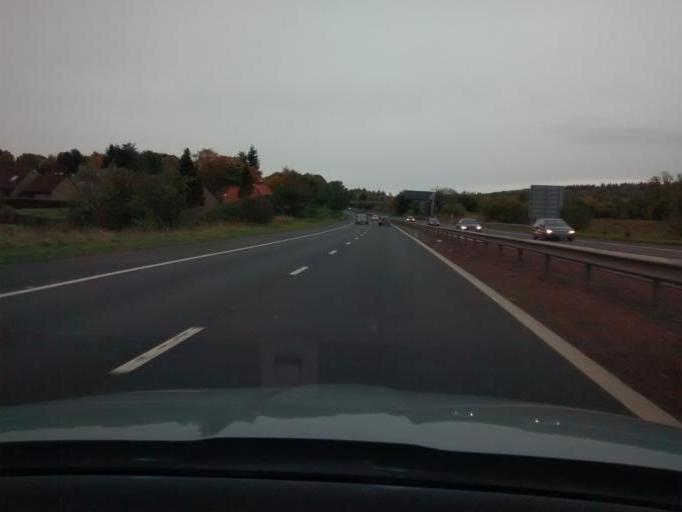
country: GB
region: Scotland
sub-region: Stirling
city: Stirling
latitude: 56.1161
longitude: -3.9674
